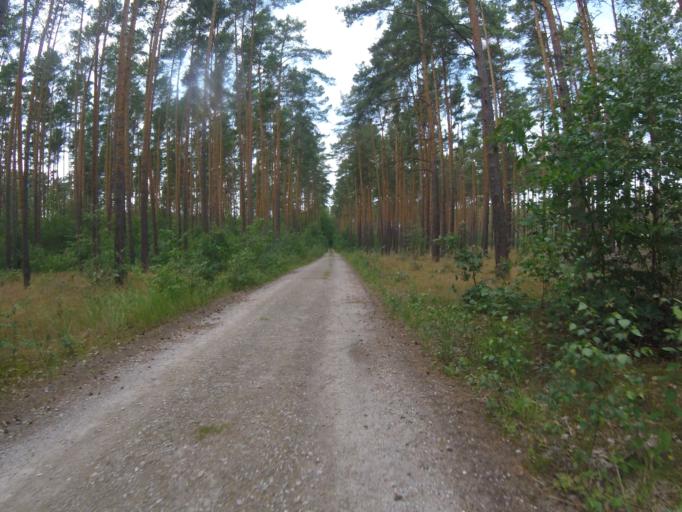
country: DE
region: Brandenburg
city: Schwerin
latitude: 52.1793
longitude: 13.5992
